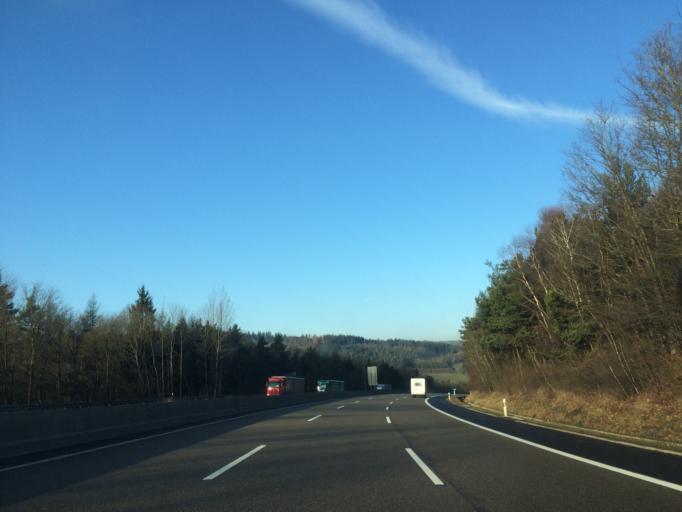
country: DE
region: Hesse
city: Schwarzenborn
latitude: 50.9599
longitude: 9.4882
